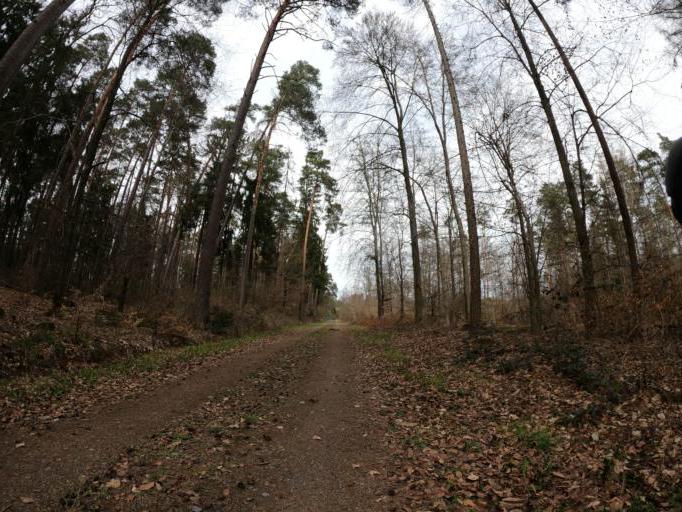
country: DE
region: Baden-Wuerttemberg
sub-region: Regierungsbezirk Stuttgart
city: Filderstadt
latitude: 48.6384
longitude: 9.1824
